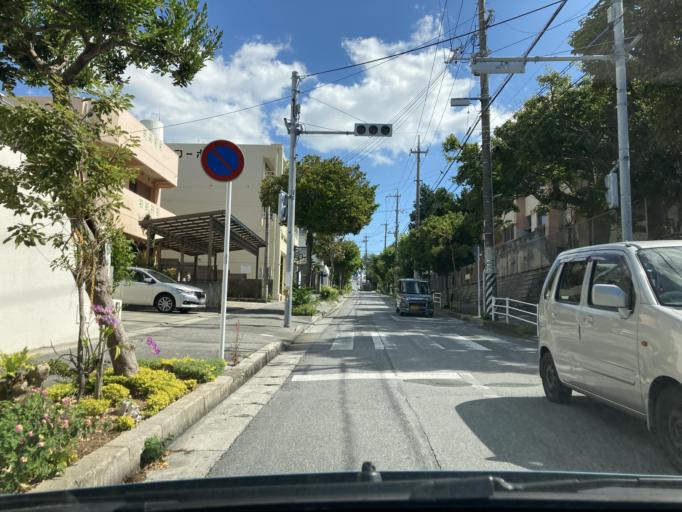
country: JP
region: Okinawa
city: Naha-shi
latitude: 26.2003
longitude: 127.6925
